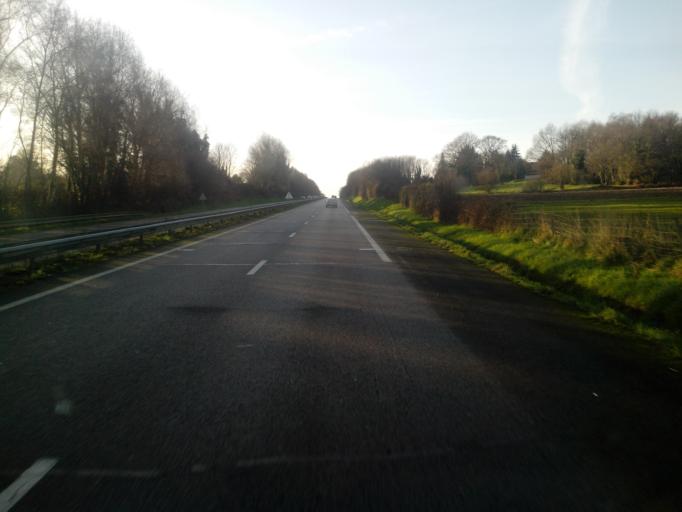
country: FR
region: Brittany
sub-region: Departement du Morbihan
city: Guenin
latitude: 47.8932
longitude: -2.9725
